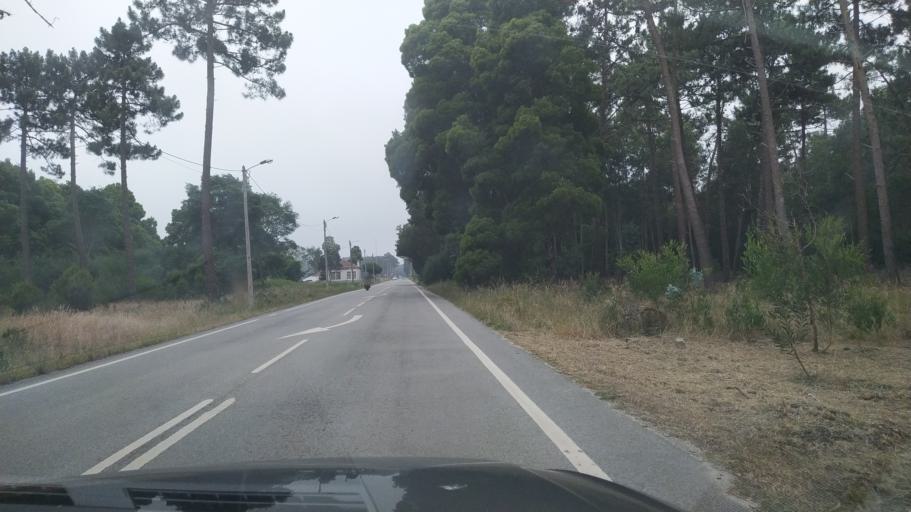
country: PT
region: Aveiro
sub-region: Ilhavo
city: Gafanha da Encarnacao
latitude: 40.6055
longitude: -8.7221
